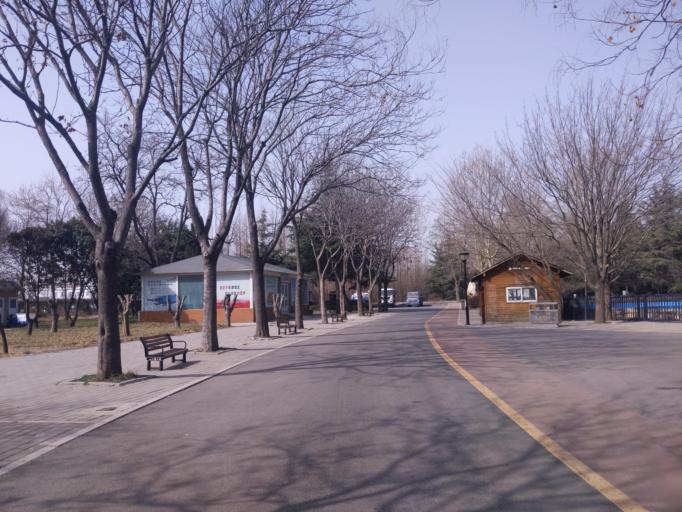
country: CN
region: Henan Sheng
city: Puyang
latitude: 35.7750
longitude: 114.9589
